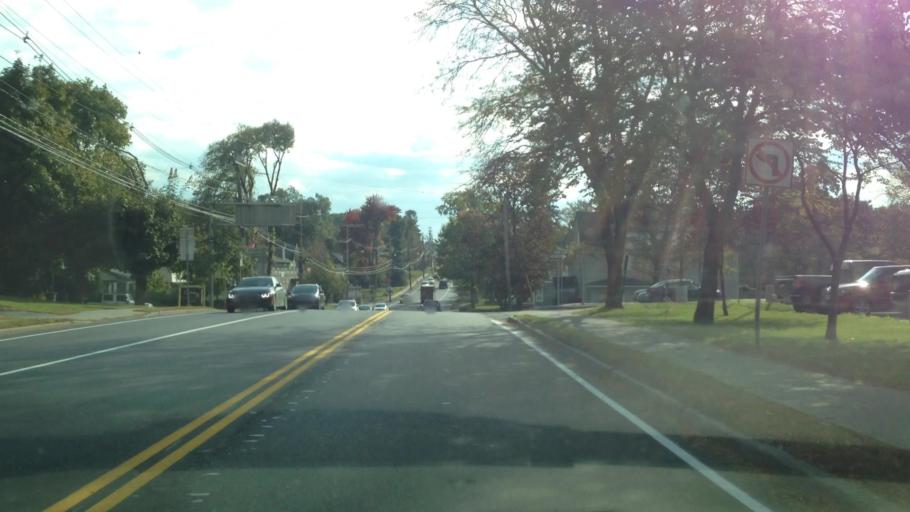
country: US
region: New York
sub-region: Ulster County
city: New Paltz
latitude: 41.7458
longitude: -74.0777
